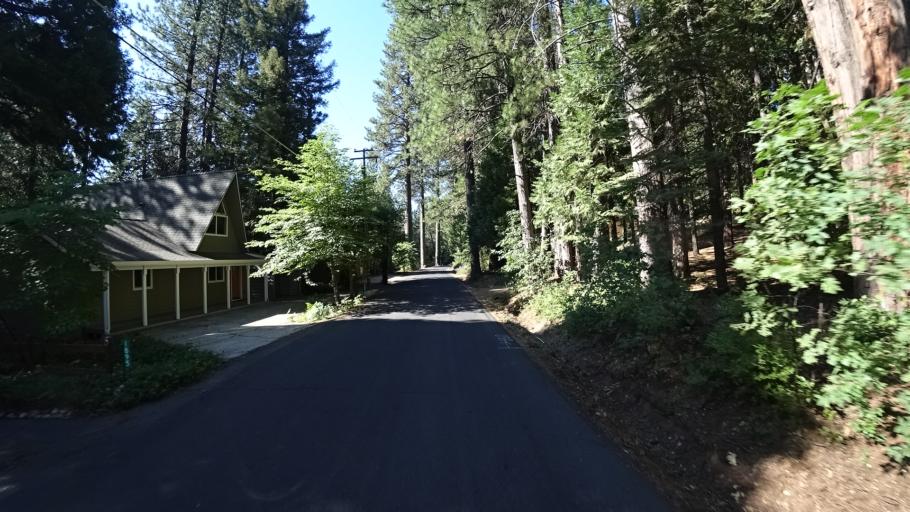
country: US
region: California
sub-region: Calaveras County
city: Arnold
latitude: 38.2481
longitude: -120.3615
